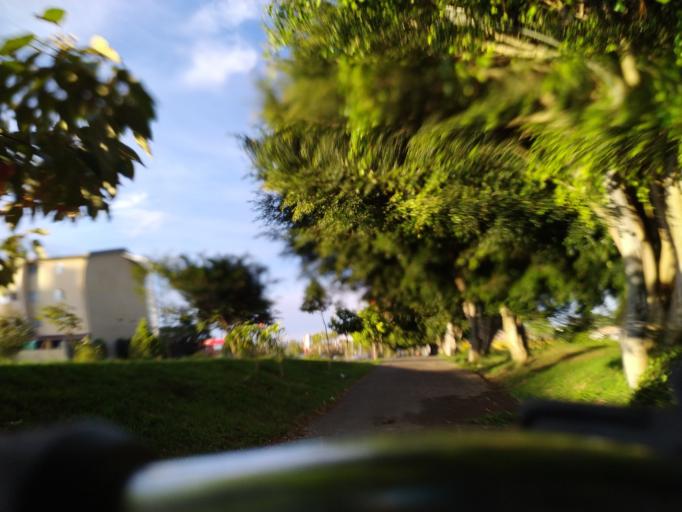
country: CO
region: Antioquia
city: Rionegro
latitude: 6.1490
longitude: -75.3734
